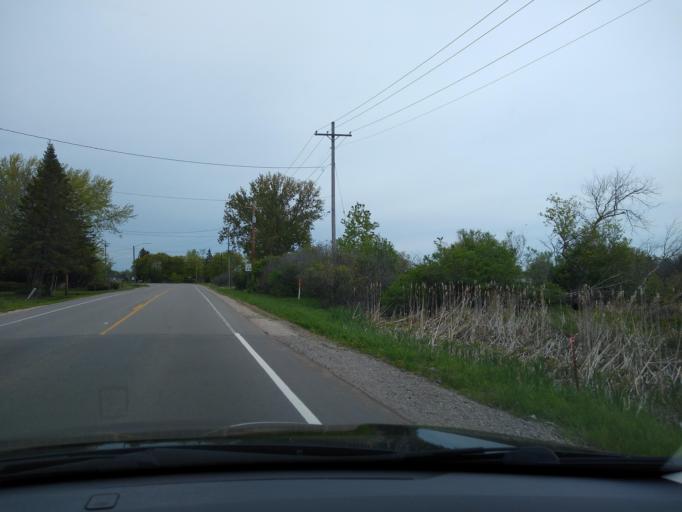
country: US
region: Michigan
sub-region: Delta County
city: Escanaba
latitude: 45.7752
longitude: -87.0703
